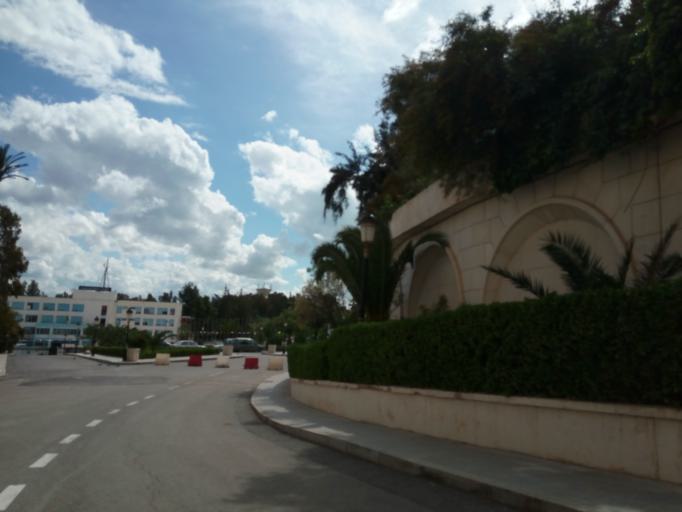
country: DZ
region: Constantine
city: Constantine
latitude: 36.3471
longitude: 6.6027
